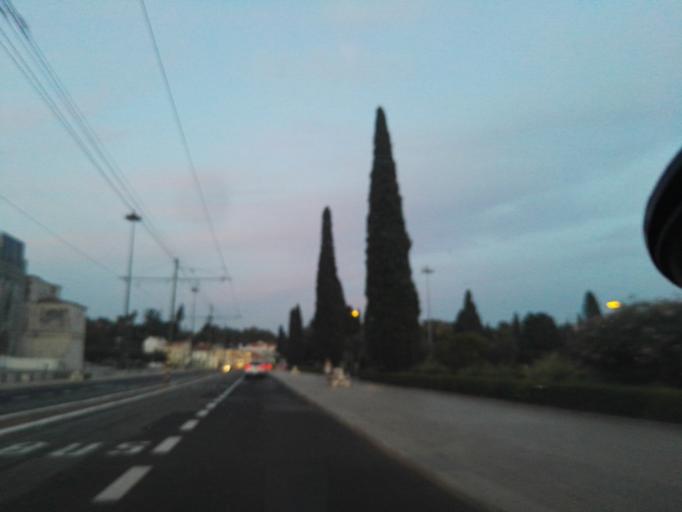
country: PT
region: Lisbon
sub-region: Oeiras
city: Alges
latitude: 38.6967
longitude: -9.2069
